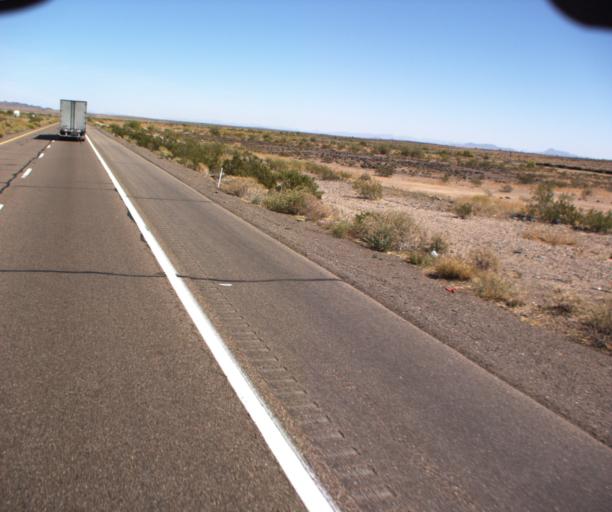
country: US
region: Arizona
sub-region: Maricopa County
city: Gila Bend
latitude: 32.8733
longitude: -113.1293
